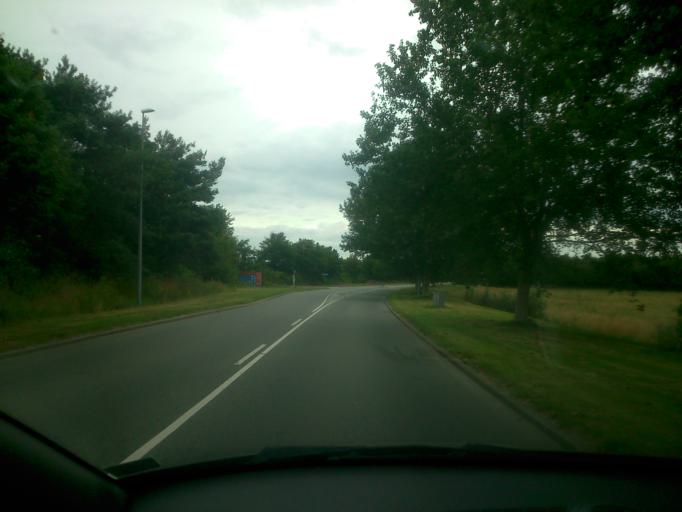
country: DK
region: South Denmark
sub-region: Esbjerg Kommune
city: Esbjerg
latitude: 55.5183
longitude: 8.4250
